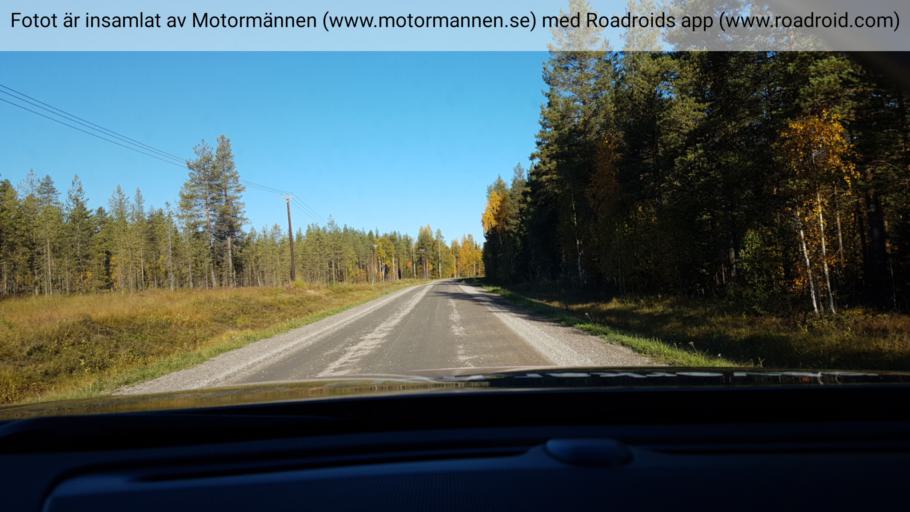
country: SE
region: Norrbotten
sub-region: Alvsbyns Kommun
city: AElvsbyn
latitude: 66.1637
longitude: 21.2480
